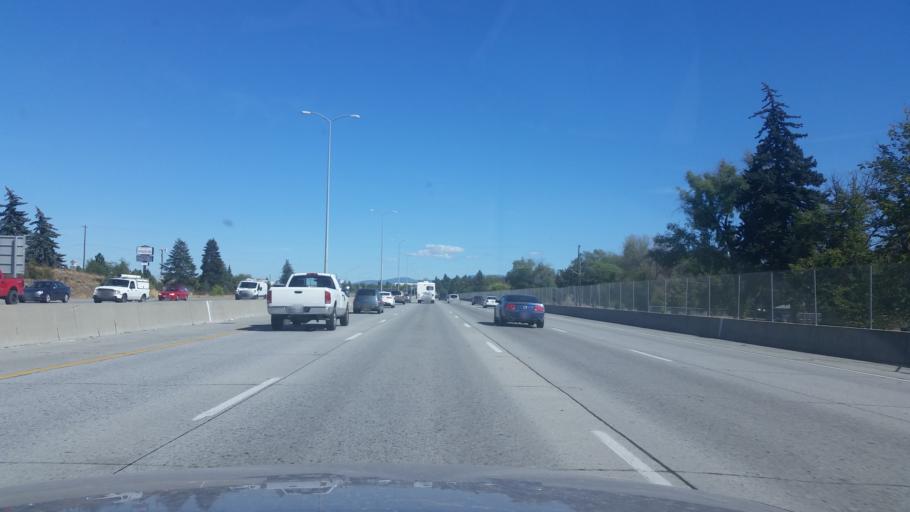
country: US
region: Washington
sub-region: Spokane County
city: Millwood
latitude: 47.6538
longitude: -117.3387
